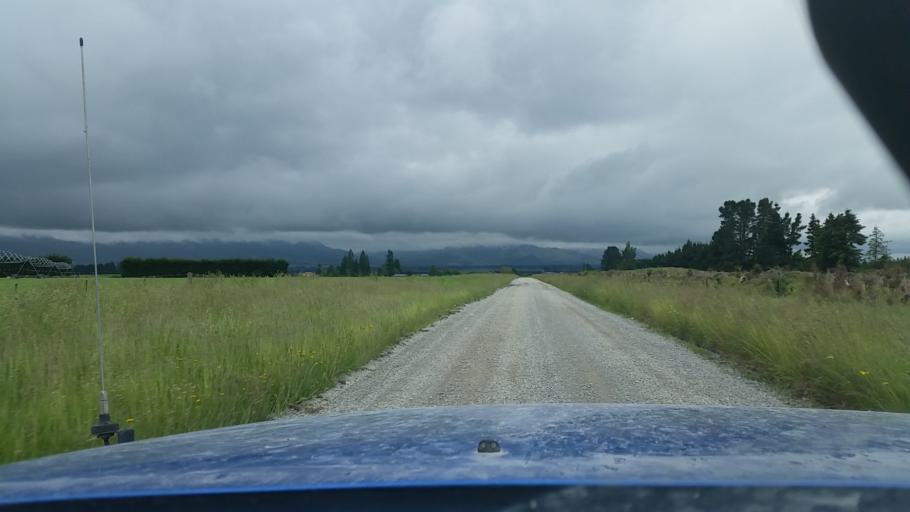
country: NZ
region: Canterbury
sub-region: Ashburton District
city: Methven
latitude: -43.7044
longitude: 171.4601
